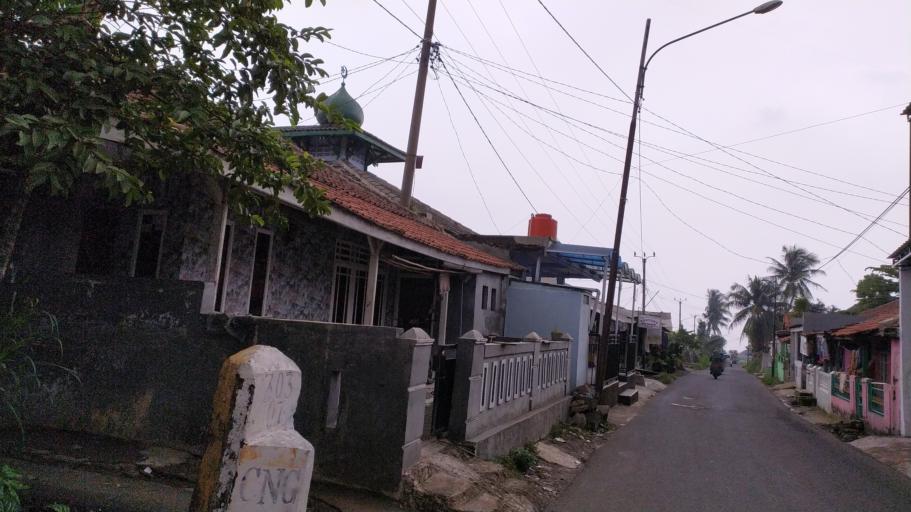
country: ID
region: West Java
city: Ciampea
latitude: -6.6123
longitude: 106.6978
